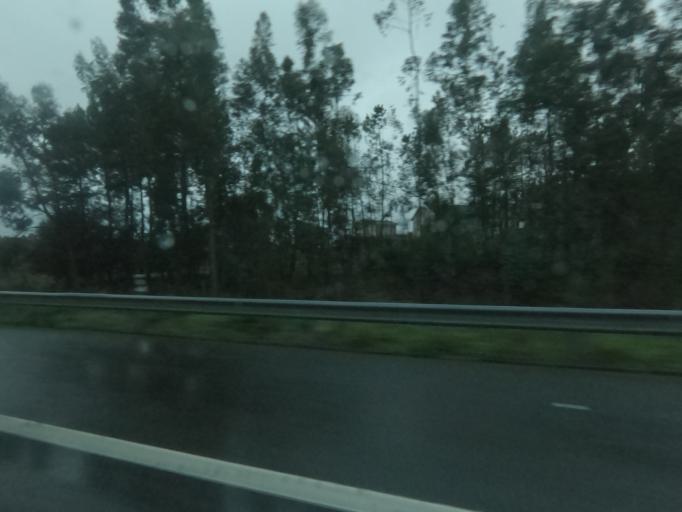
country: PT
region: Braga
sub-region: Braga
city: Oliveira
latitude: 41.5314
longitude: -8.4836
